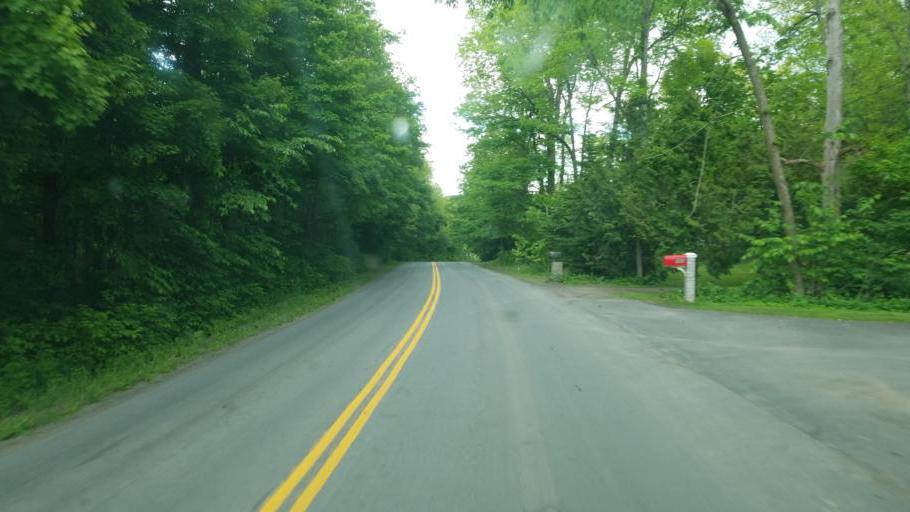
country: US
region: New York
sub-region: Oneida County
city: Chadwicks
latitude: 42.9314
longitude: -75.2023
